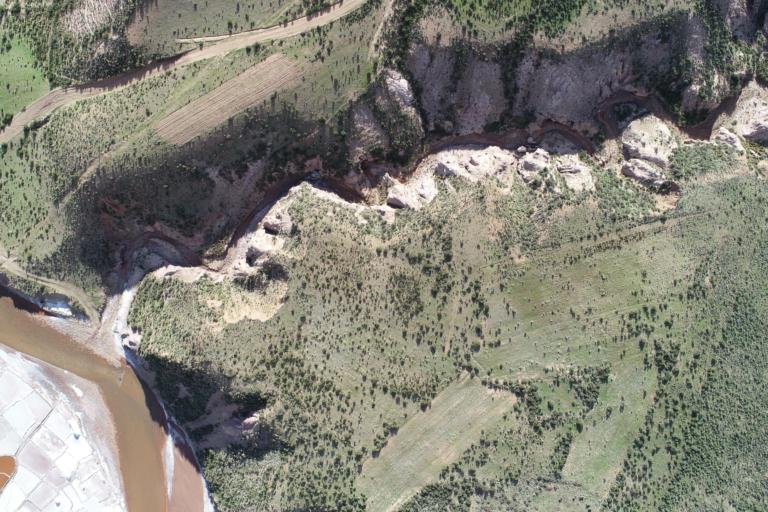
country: BO
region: La Paz
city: Curahuara de Carangas
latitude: -17.2991
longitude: -68.4888
